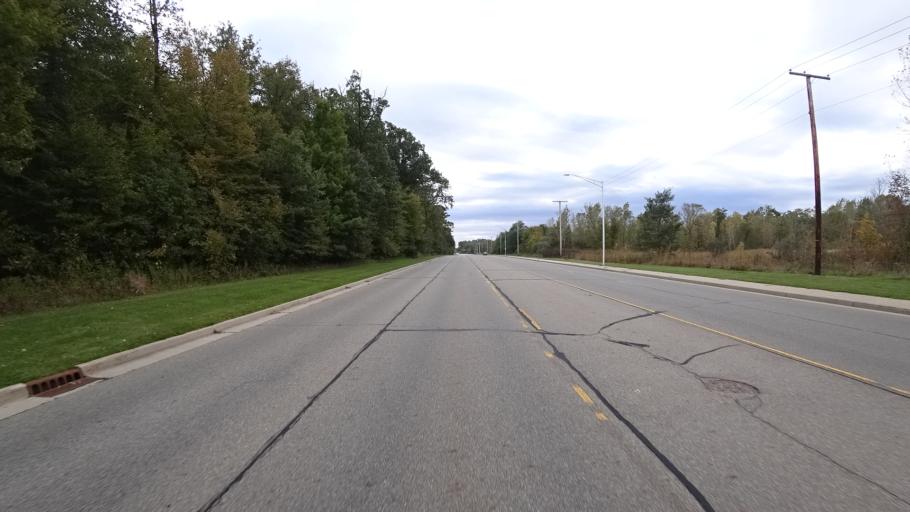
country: US
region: Indiana
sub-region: LaPorte County
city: Trail Creek
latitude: 41.6701
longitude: -86.8845
